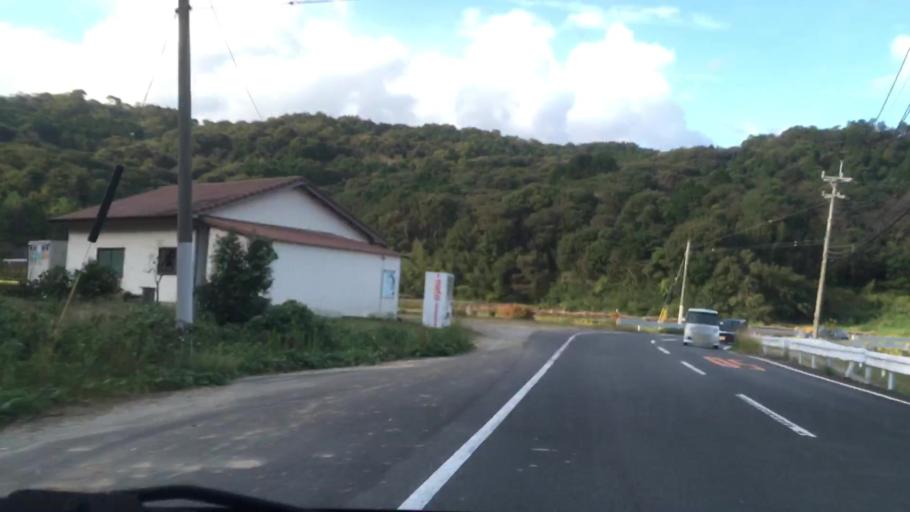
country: JP
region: Nagasaki
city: Sasebo
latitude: 32.9549
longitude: 129.6755
